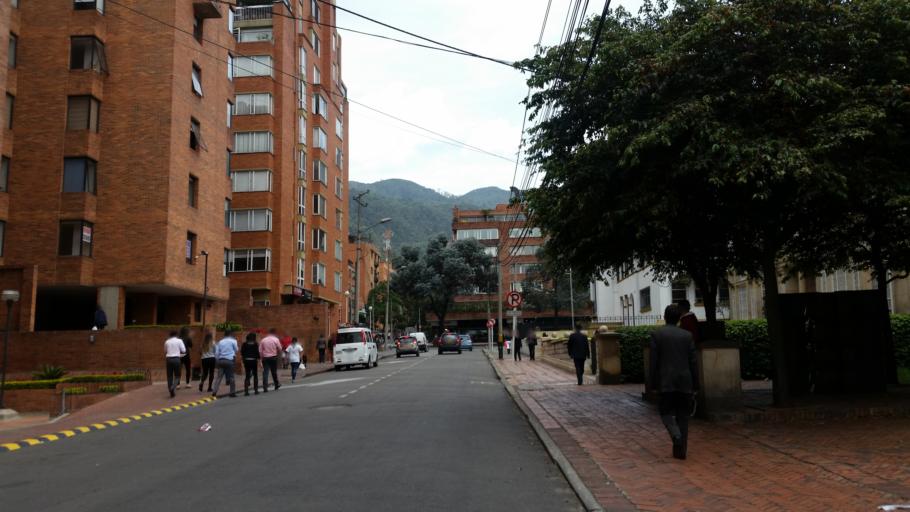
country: CO
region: Bogota D.C.
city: Barrio San Luis
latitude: 4.6540
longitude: -74.0568
